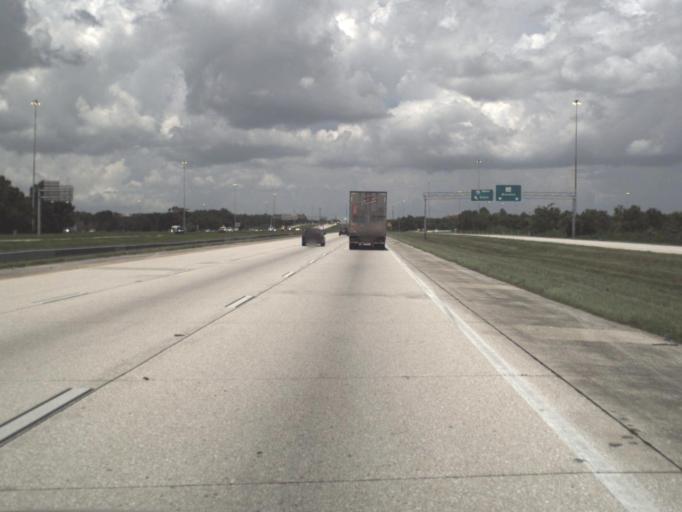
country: US
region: Florida
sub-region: Hillsborough County
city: Brandon
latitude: 27.9311
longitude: -82.3306
